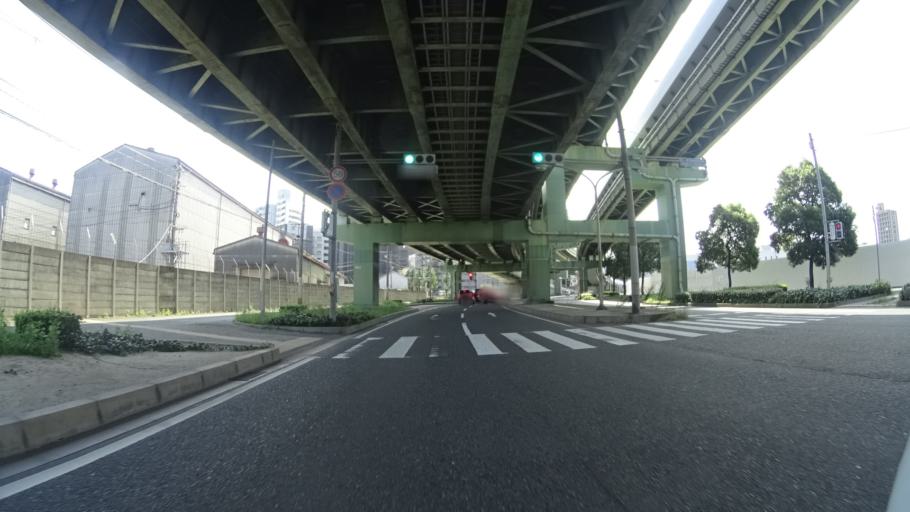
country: JP
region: Fukuoka
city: Kitakyushu
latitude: 33.8815
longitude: 130.8600
